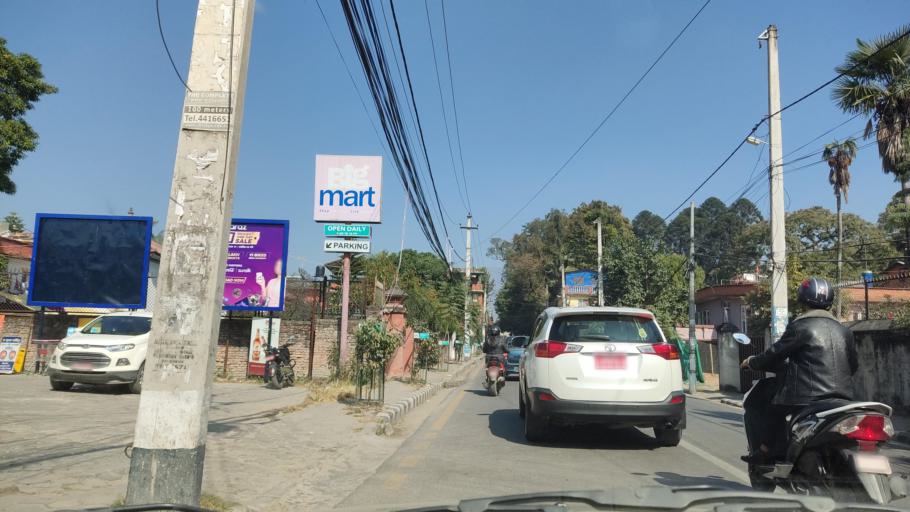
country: NP
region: Central Region
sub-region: Bagmati Zone
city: Kathmandu
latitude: 27.7187
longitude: 85.3336
